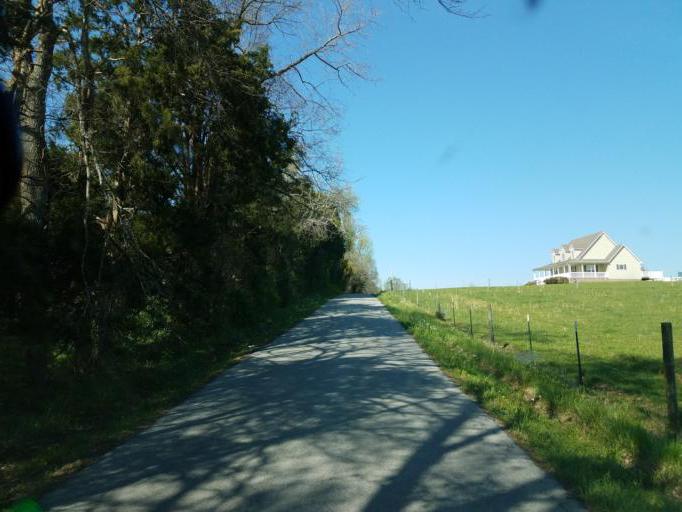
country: US
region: Kentucky
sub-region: Edmonson County
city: Brownsville
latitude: 37.1239
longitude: -86.1500
